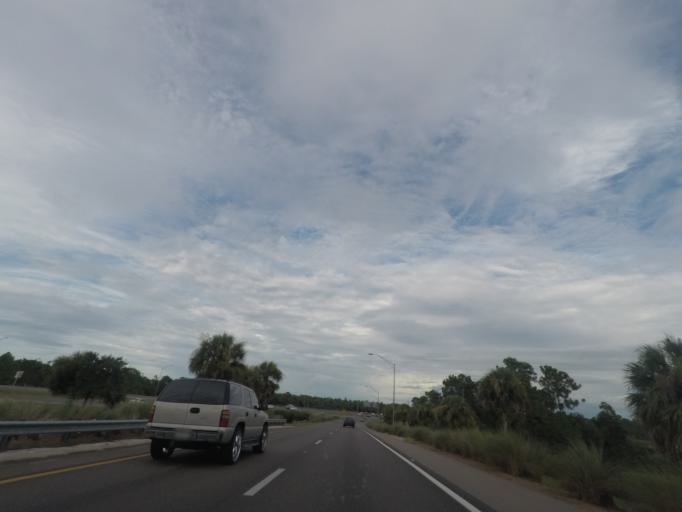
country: US
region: Florida
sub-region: Orange County
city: Hunters Creek
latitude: 28.3563
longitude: -81.4792
